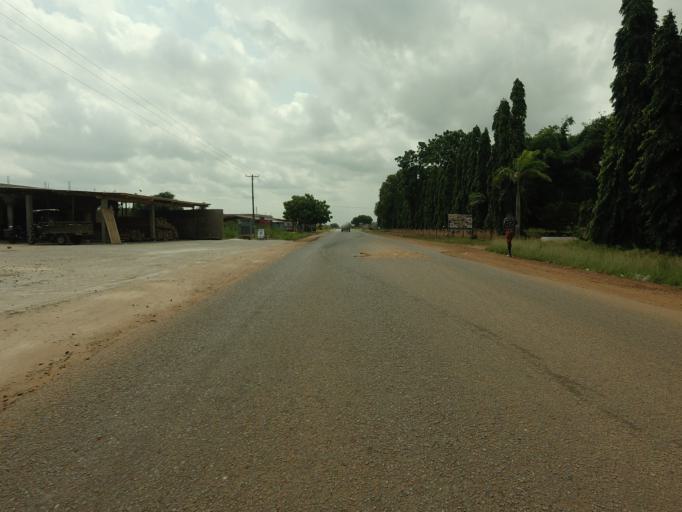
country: TG
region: Maritime
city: Lome
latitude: 6.1305
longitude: 1.1215
